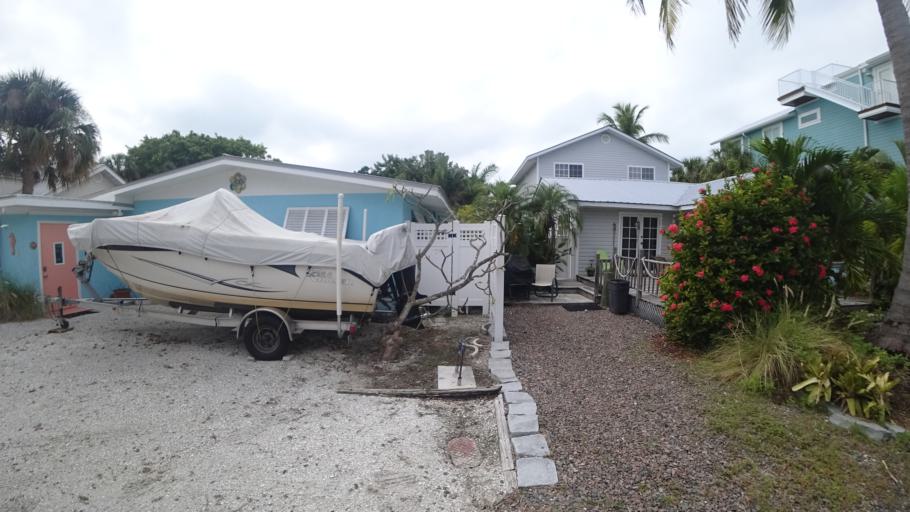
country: US
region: Florida
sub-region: Manatee County
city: Bradenton Beach
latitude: 27.4800
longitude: -82.7022
